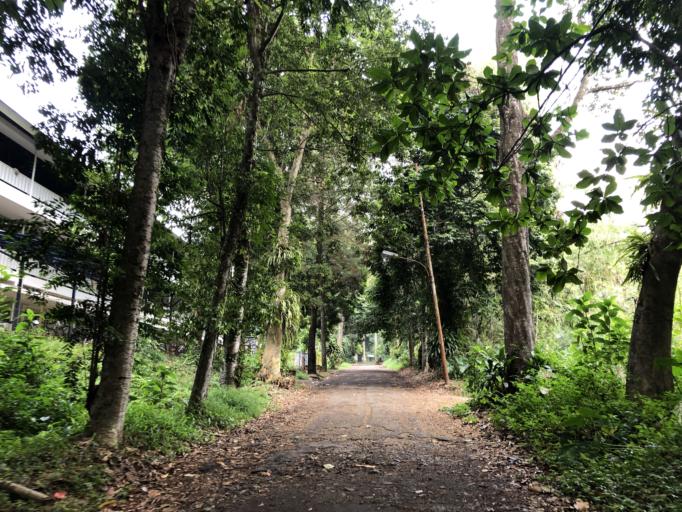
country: ID
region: West Java
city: Ciampea
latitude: -6.5550
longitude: 106.7230
